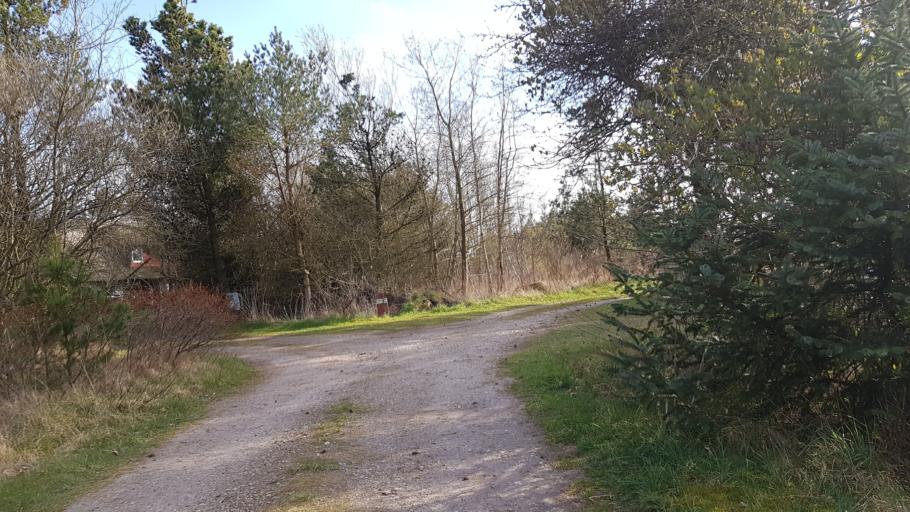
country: DE
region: Schleswig-Holstein
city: List
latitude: 55.1287
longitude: 8.5270
